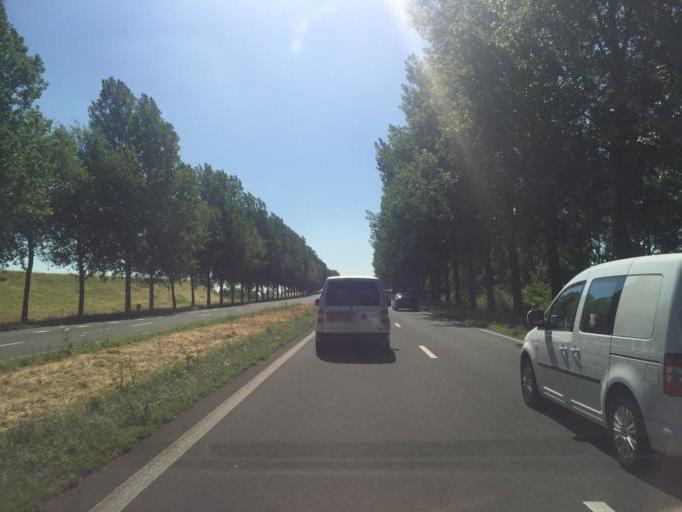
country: NL
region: North Holland
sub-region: Gemeente Haarlemmermeer
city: Hoofddorp
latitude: 52.3161
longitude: 4.6953
